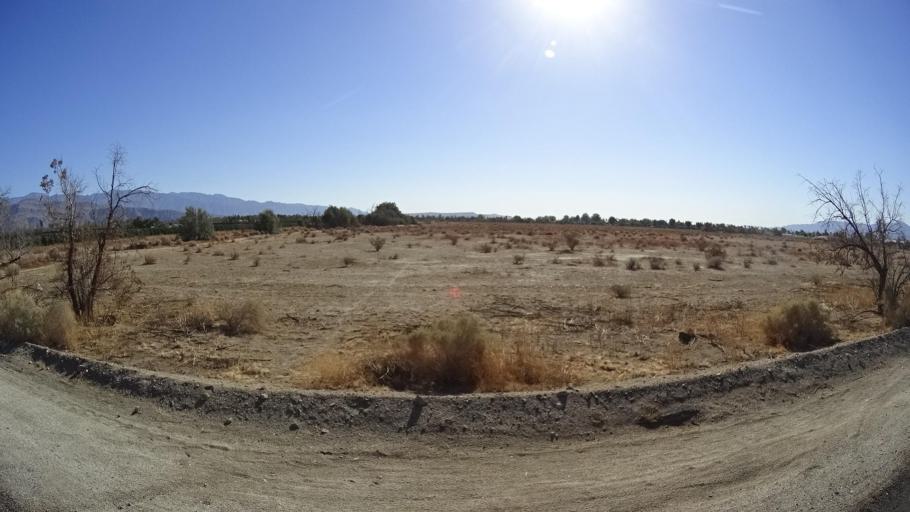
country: US
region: California
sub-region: San Diego County
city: Borrego Springs
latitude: 33.2663
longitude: -116.3750
